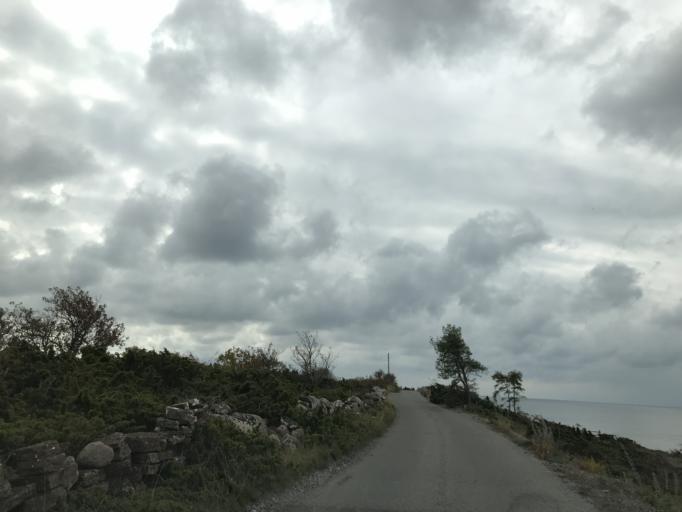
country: SE
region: Kalmar
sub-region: Borgholms Kommun
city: Borgholm
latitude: 57.0431
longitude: 16.8277
